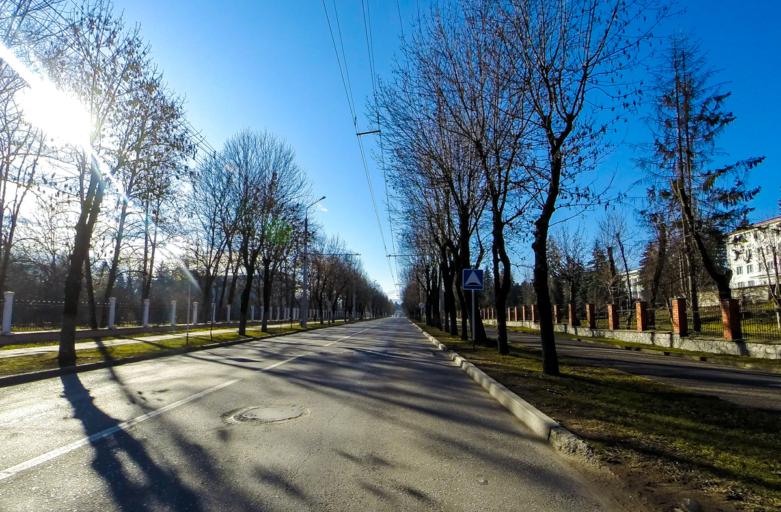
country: RU
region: Kabardino-Balkariya
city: Vol'nyy Aul
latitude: 43.4579
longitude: 43.5842
